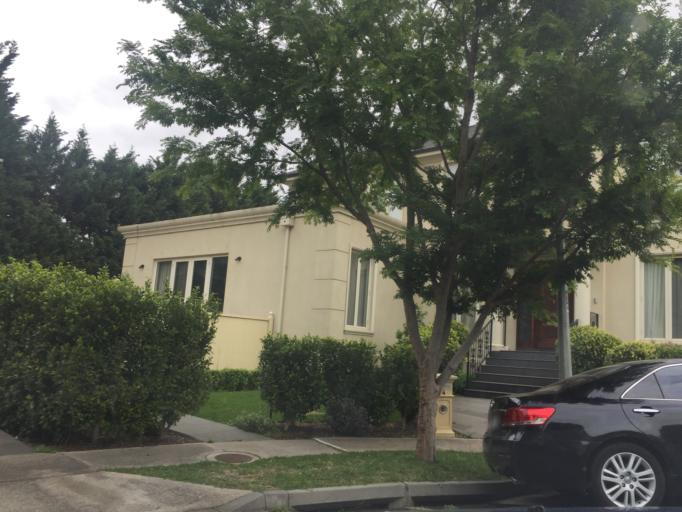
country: AU
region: Victoria
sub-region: Boroondara
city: Hawthorn East
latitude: -37.8173
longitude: 145.0513
